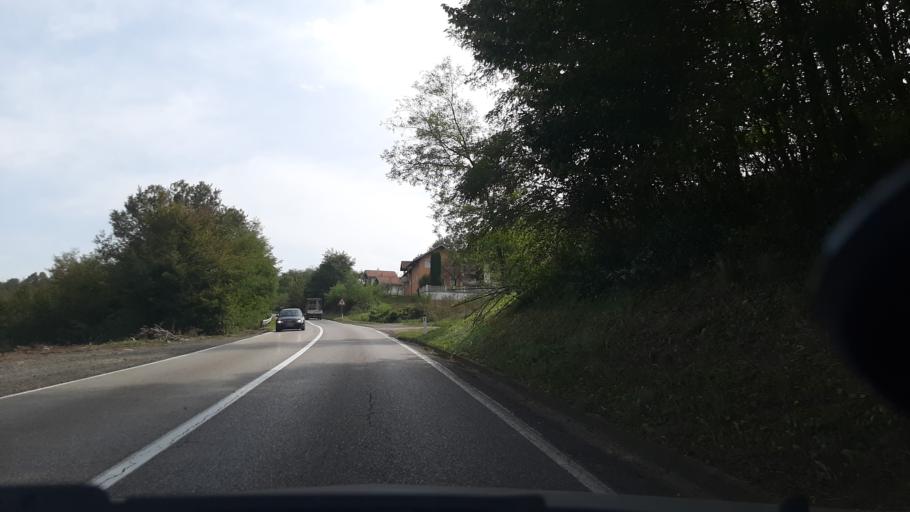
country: BA
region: Republika Srpska
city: Laktasi
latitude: 44.8700
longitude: 17.3357
